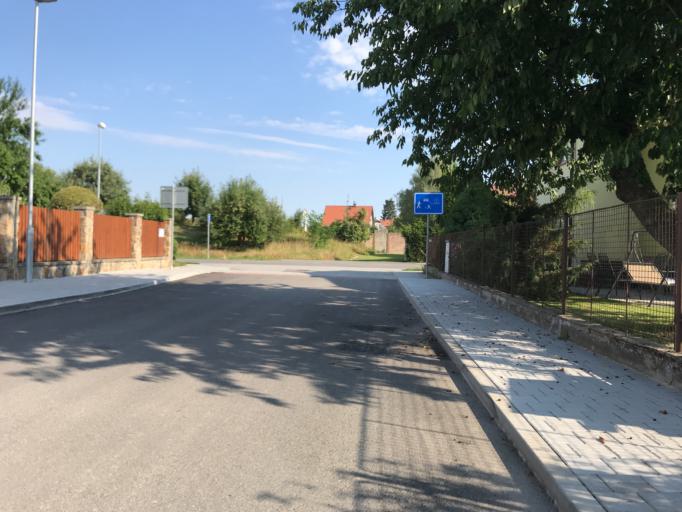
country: CZ
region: Jihocesky
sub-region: Okres Jindrichuv Hradec
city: Trebon
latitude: 49.0066
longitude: 14.7532
